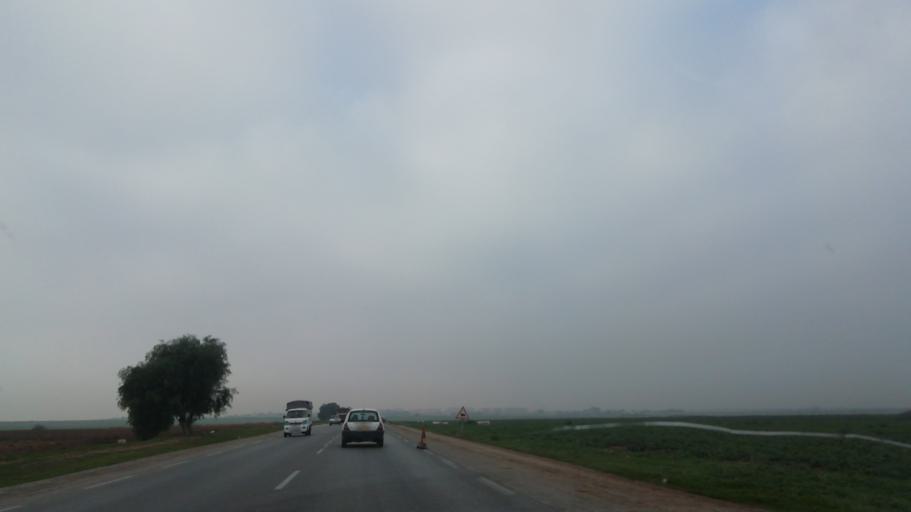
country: DZ
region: Relizane
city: Djidiouia
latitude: 35.8983
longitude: 0.7568
